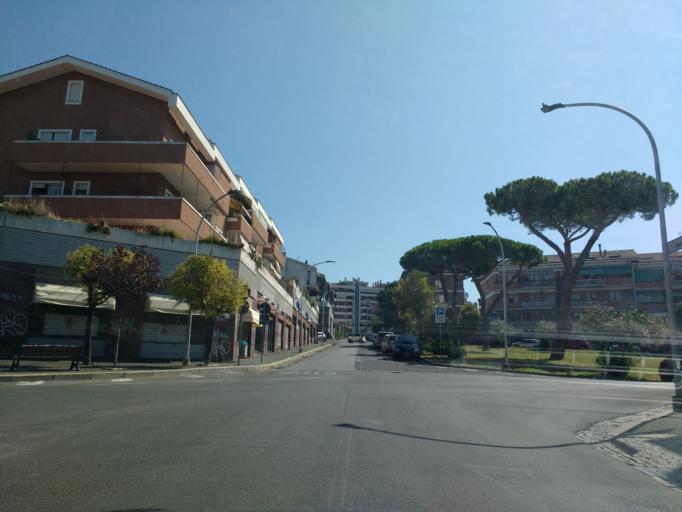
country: IT
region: Latium
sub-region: Citta metropolitana di Roma Capitale
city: Acilia-Castel Fusano-Ostia Antica
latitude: 41.7704
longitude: 12.3711
